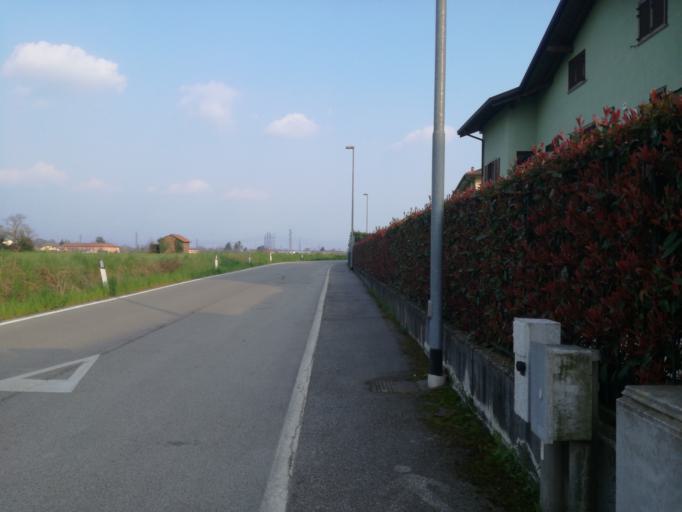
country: IT
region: Lombardy
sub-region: Provincia di Lecco
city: Verderio Superiore
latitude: 45.6641
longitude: 9.4396
